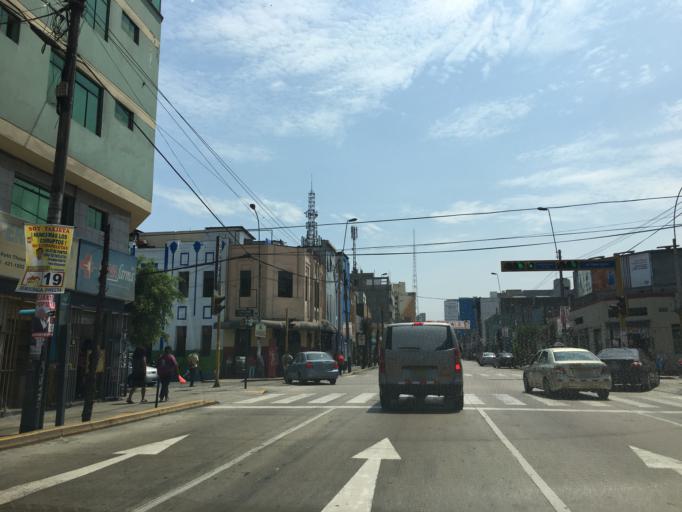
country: PE
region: Lima
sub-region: Lima
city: San Isidro
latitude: -12.0871
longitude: -77.0329
